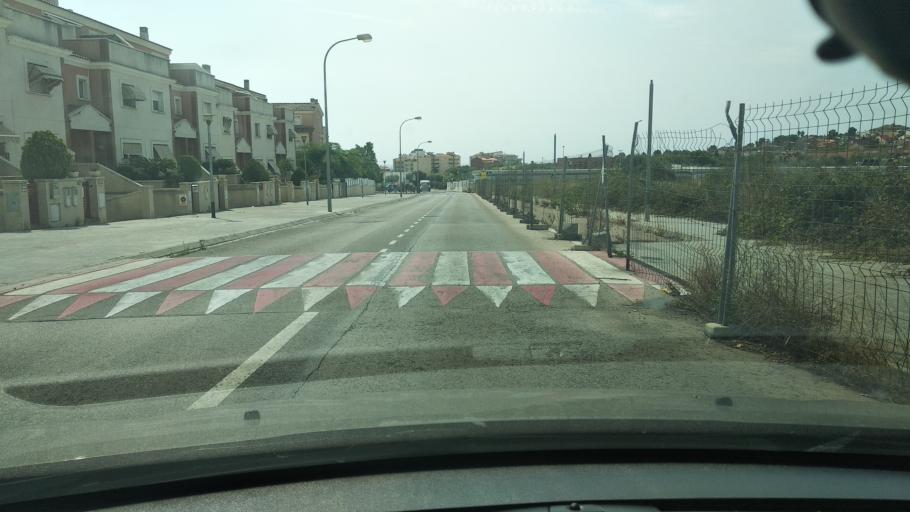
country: ES
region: Catalonia
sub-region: Provincia de Tarragona
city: El Vendrell
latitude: 41.2182
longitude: 1.5240
